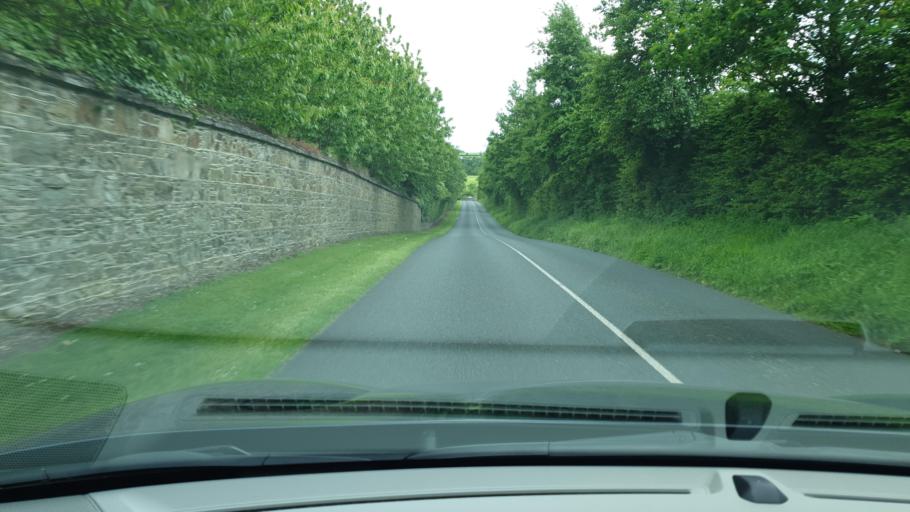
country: IE
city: Kilquade
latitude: 53.0965
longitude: -6.0844
